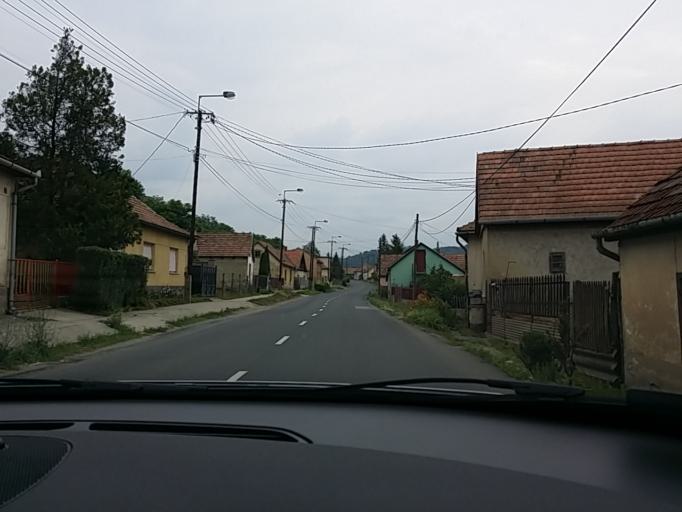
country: HU
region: Nograd
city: Batonyterenye
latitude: 48.0059
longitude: 19.8375
